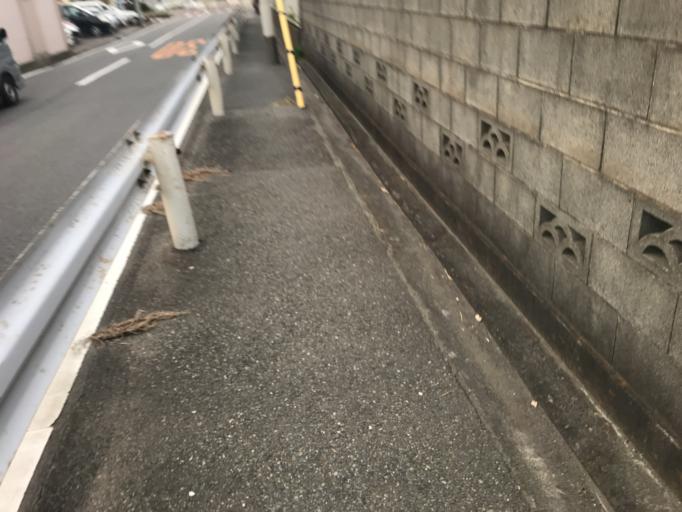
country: JP
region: Kanagawa
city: Fujisawa
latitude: 35.3185
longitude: 139.4675
